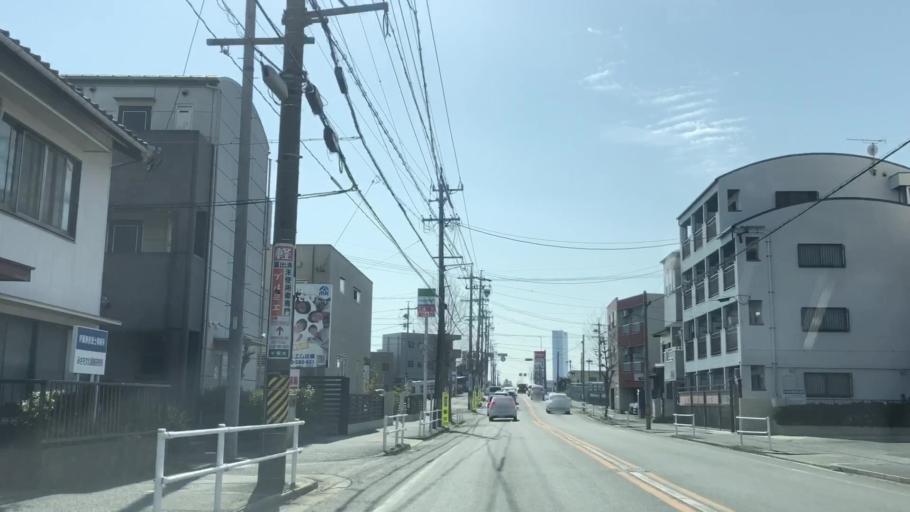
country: JP
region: Aichi
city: Toyohashi
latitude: 34.7544
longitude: 137.3798
